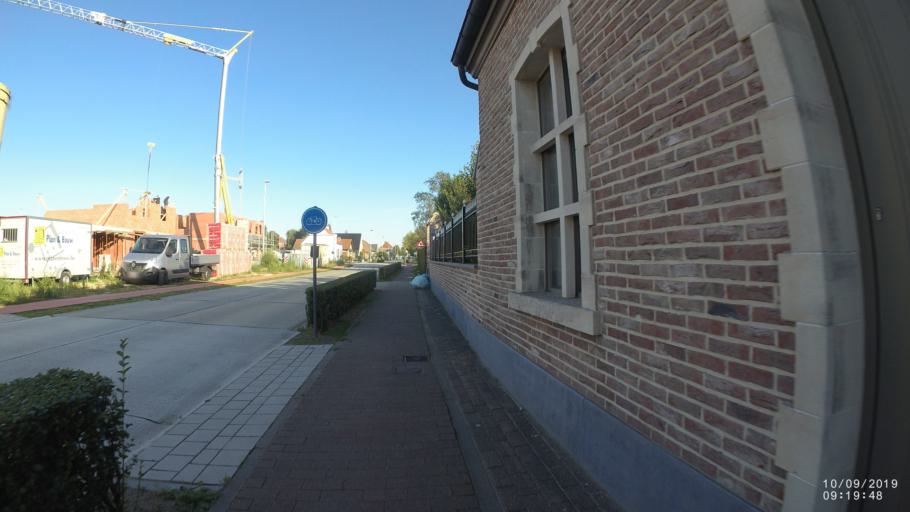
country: BE
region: Flanders
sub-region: Provincie Oost-Vlaanderen
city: Lochristi
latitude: 51.0943
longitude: 3.8402
